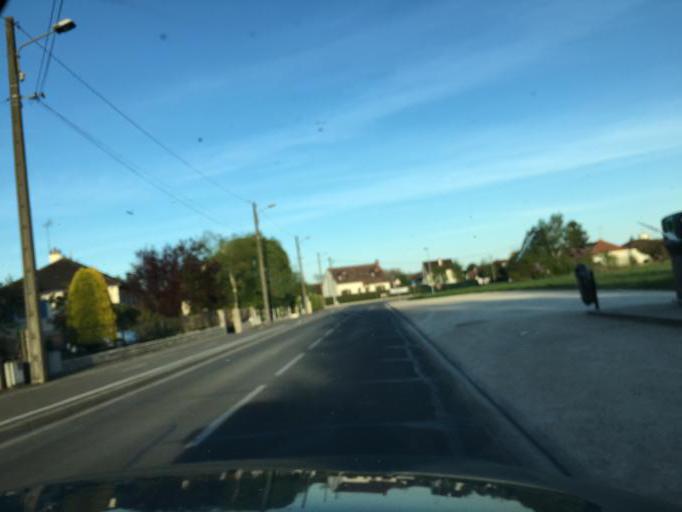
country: FR
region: Centre
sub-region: Departement du Loiret
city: Saint-Jean-le-Blanc
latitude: 47.8827
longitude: 1.9377
